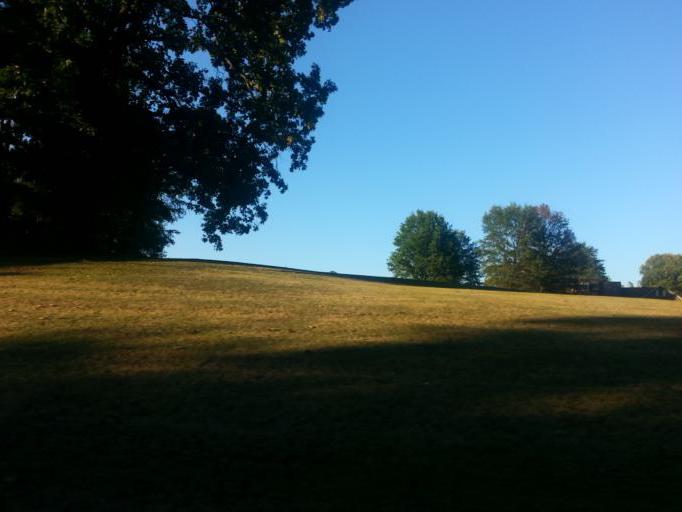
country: US
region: Tennessee
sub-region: Blount County
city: Wildwood
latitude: 35.8564
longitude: -83.8808
